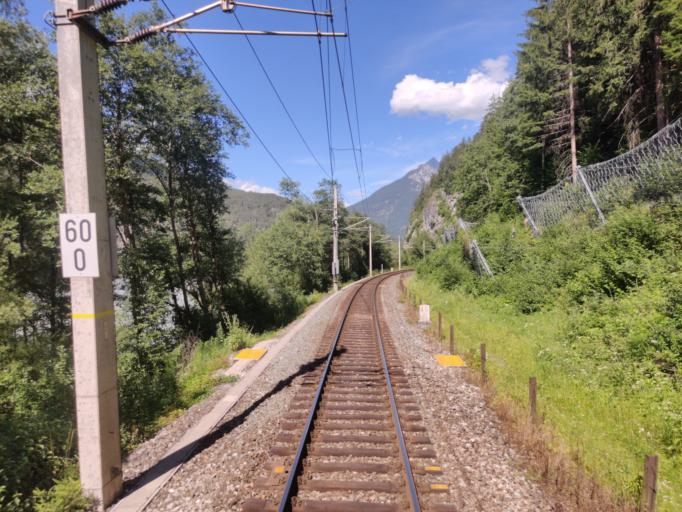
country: AT
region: Tyrol
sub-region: Politischer Bezirk Imst
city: Imsterberg
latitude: 47.2080
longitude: 10.6947
